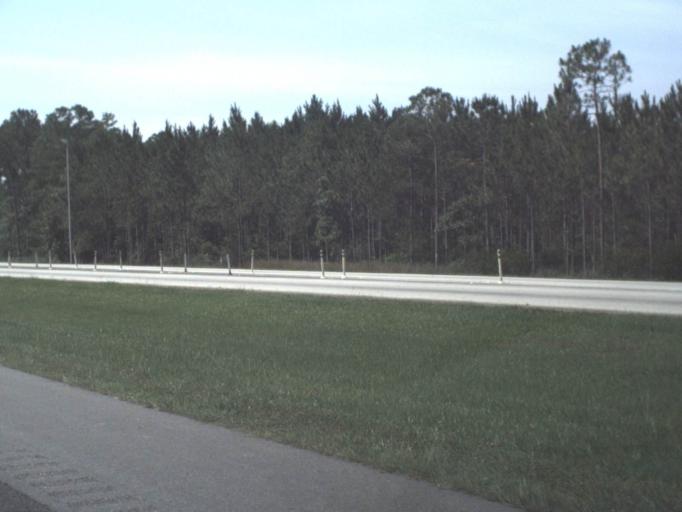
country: US
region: Florida
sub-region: Nassau County
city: Yulee
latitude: 30.6729
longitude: -81.6690
